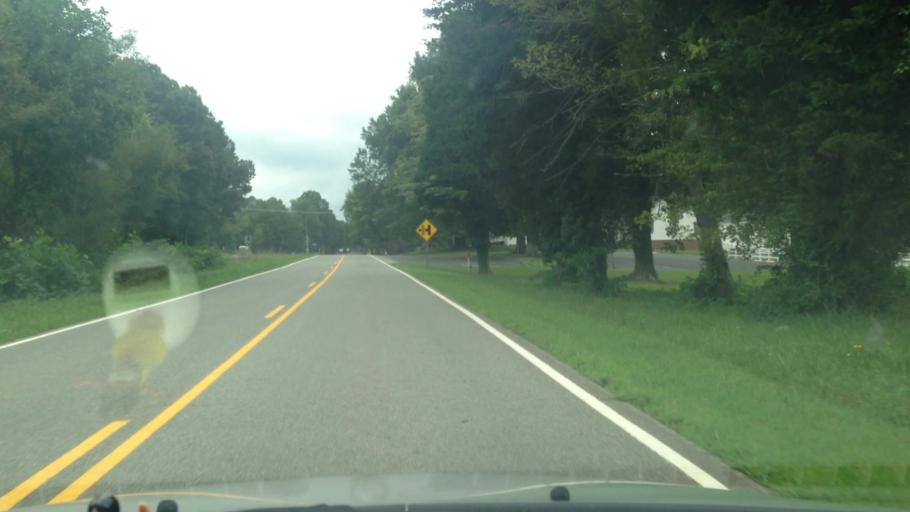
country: US
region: North Carolina
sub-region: Stokes County
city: Walnut Cove
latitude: 36.2619
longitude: -80.1467
